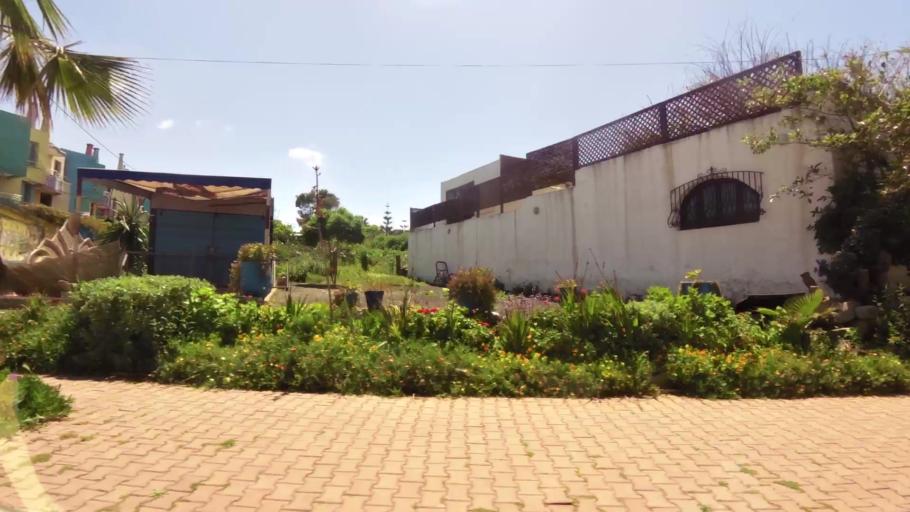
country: MA
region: Grand Casablanca
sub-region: Nouaceur
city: Dar Bouazza
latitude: 33.5331
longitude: -7.8256
